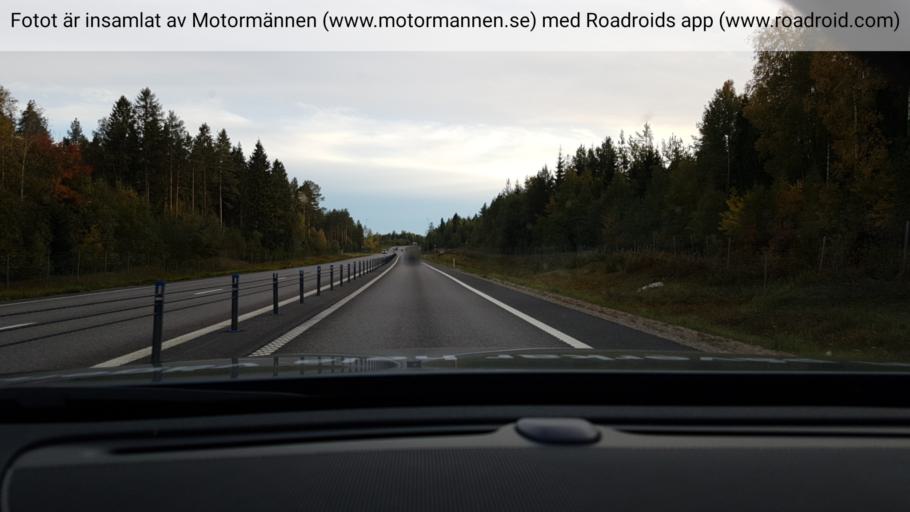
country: SE
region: Vaesternorrland
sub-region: Sundsvalls Kommun
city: Njurundabommen
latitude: 62.1360
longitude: 17.3382
